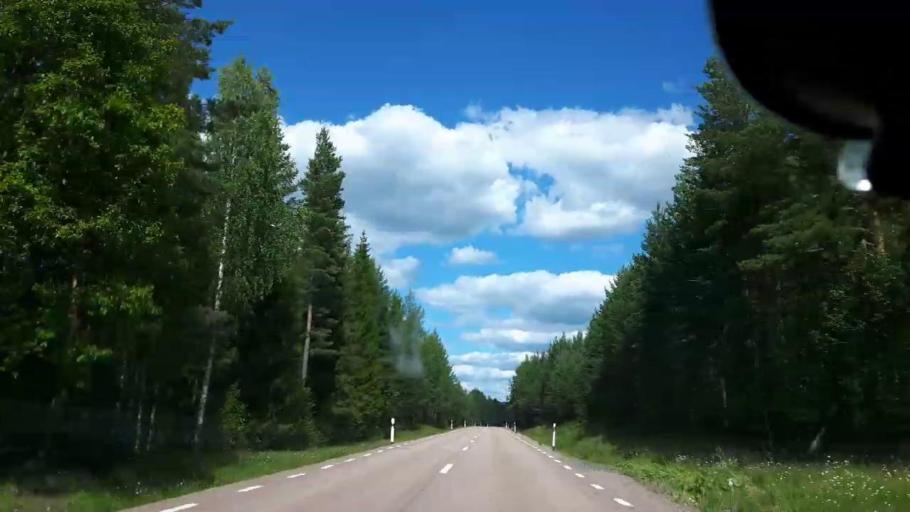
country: SE
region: Jaemtland
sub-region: Ragunda Kommun
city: Hammarstrand
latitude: 62.9103
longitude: 16.7023
